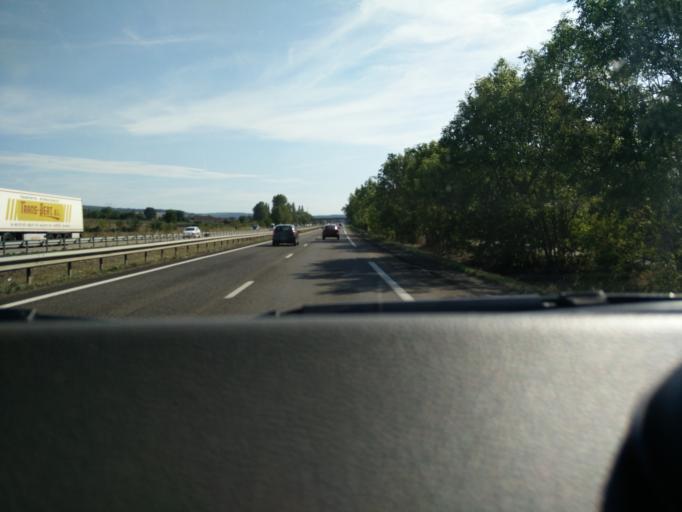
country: FR
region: Lorraine
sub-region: Departement de Meurthe-et-Moselle
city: Dieulouard
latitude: 48.8734
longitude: 6.0954
